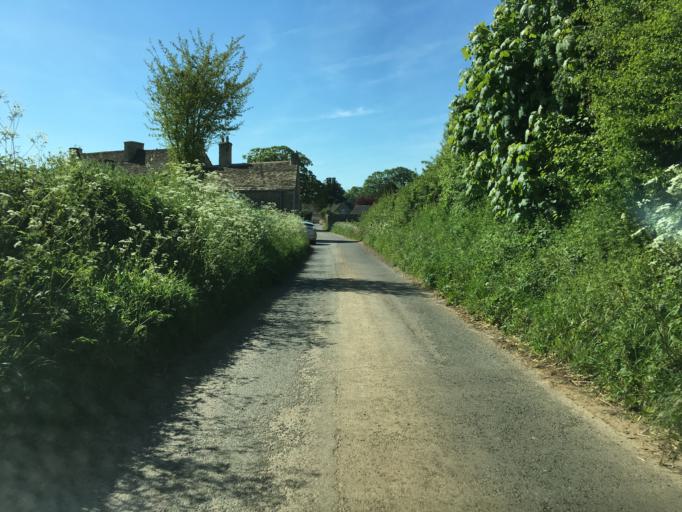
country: GB
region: England
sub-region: Wiltshire
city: Luckington
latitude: 51.6215
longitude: -2.2572
